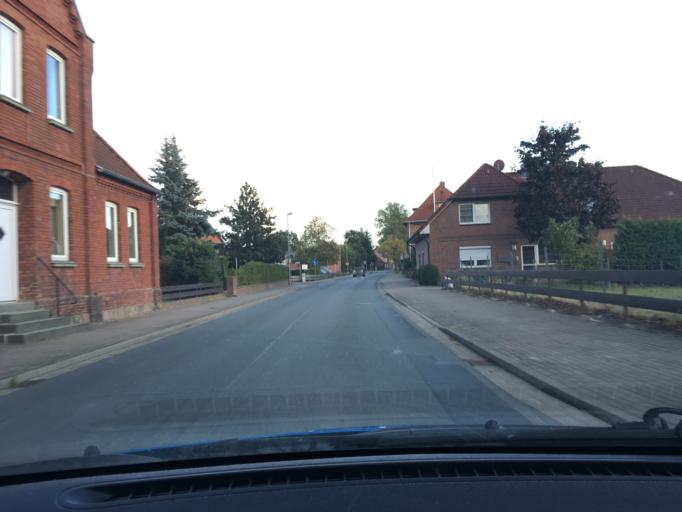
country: DE
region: Lower Saxony
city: Bleckede
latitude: 53.2963
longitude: 10.7232
